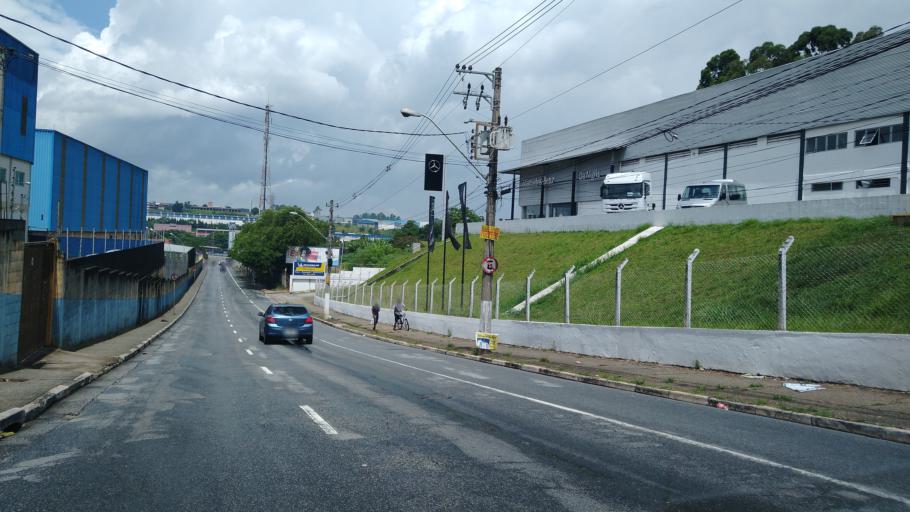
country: BR
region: Sao Paulo
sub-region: Itaquaquecetuba
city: Itaquaquecetuba
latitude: -23.4333
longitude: -46.4085
